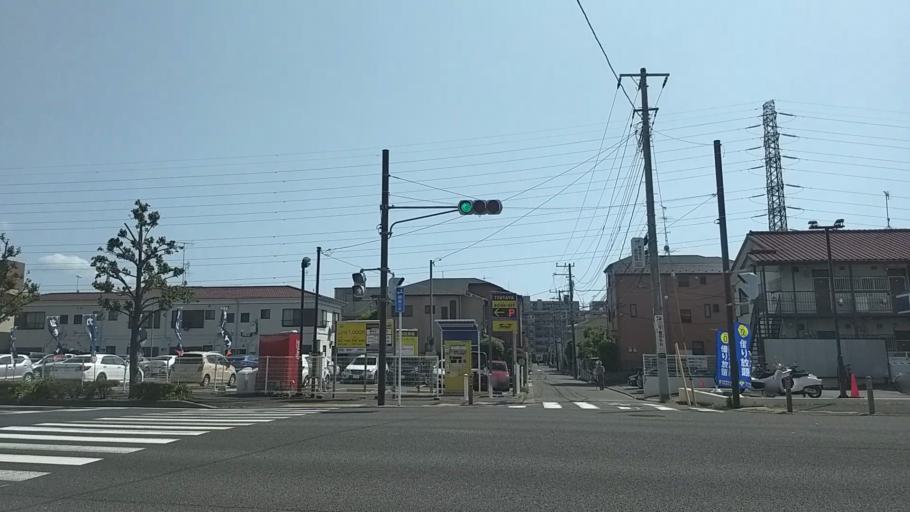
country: JP
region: Kanagawa
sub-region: Kawasaki-shi
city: Kawasaki
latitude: 35.5480
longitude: 139.6292
